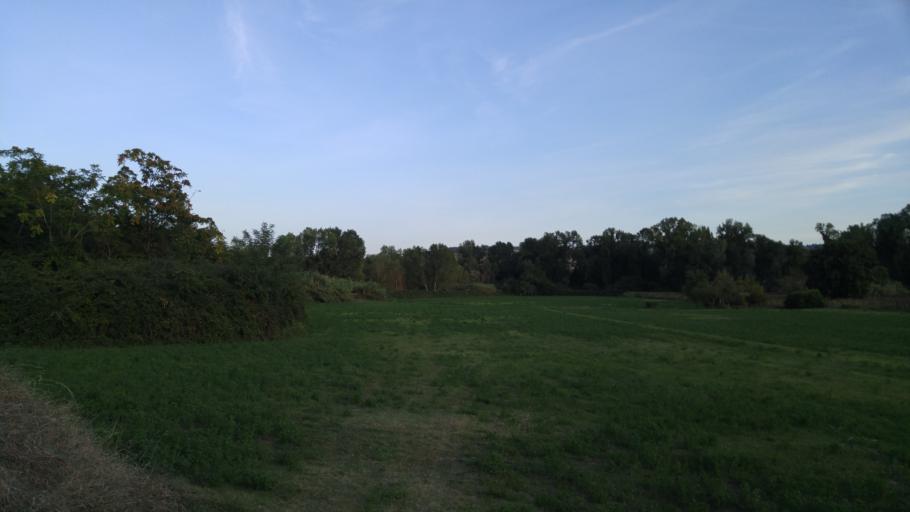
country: IT
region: The Marches
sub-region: Provincia di Pesaro e Urbino
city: Lucrezia
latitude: 43.7631
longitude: 12.9448
